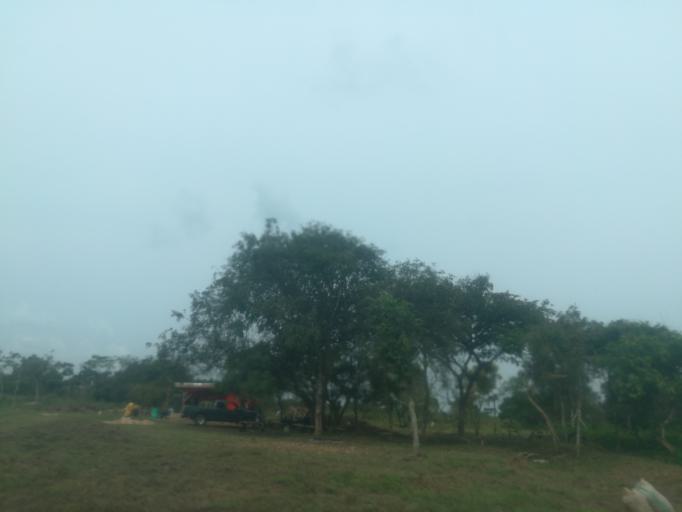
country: NG
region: Ogun
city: Ayetoro
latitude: 7.2730
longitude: 3.1006
